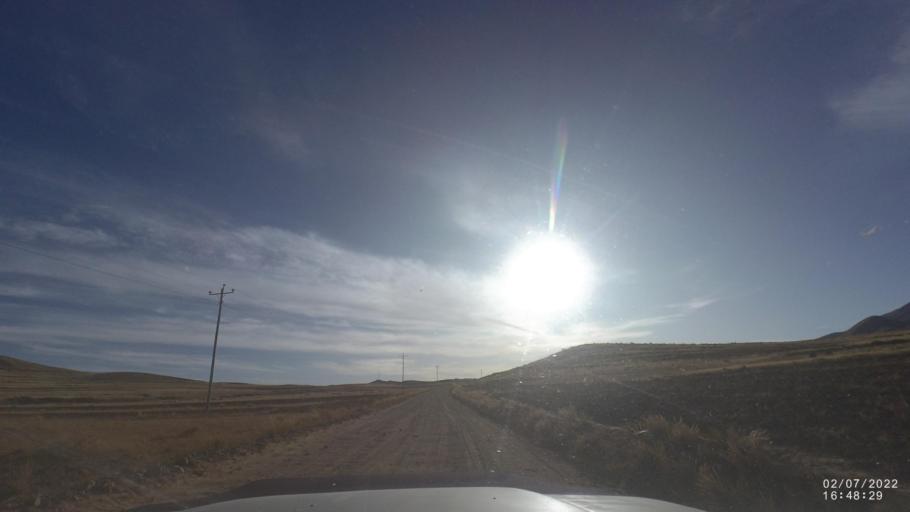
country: BO
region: Cochabamba
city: Irpa Irpa
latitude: -17.9779
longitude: -66.5192
